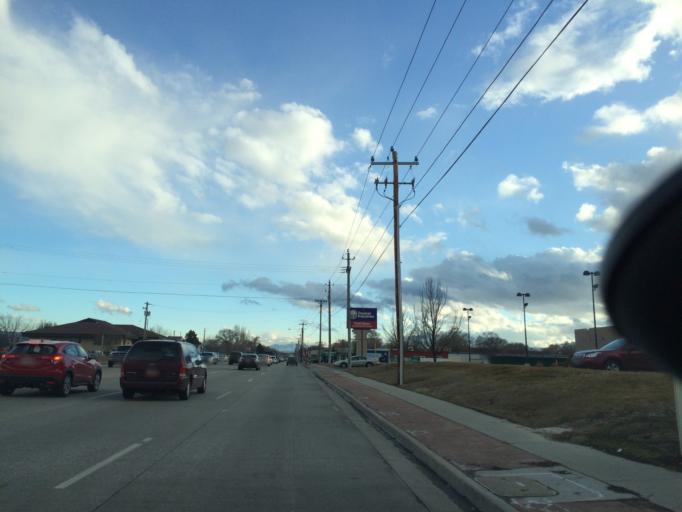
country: US
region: Utah
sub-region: Salt Lake County
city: West Jordan
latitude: 40.6215
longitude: -111.9389
